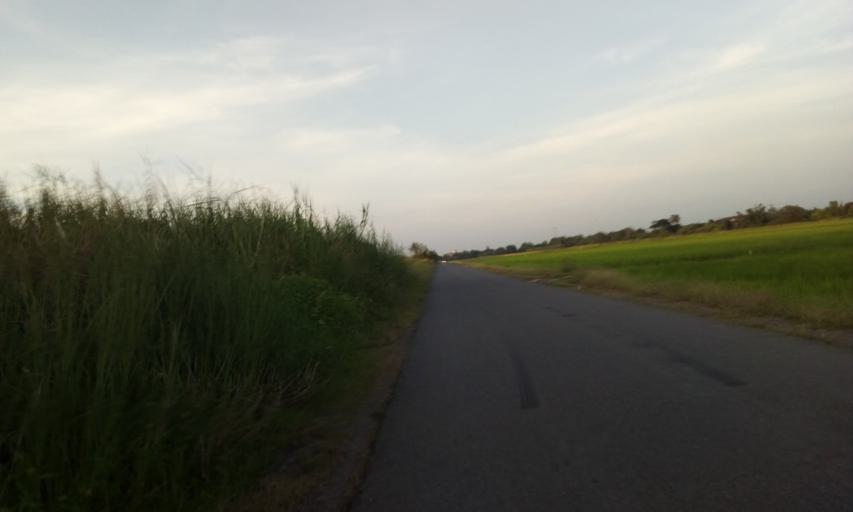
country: TH
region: Pathum Thani
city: Nong Suea
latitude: 14.0571
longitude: 100.8675
